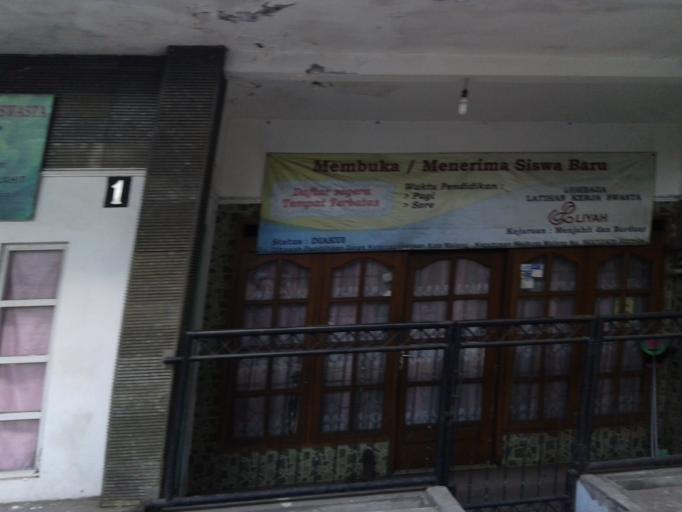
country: ID
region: East Java
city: Singosari
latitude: -7.9311
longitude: 112.6477
